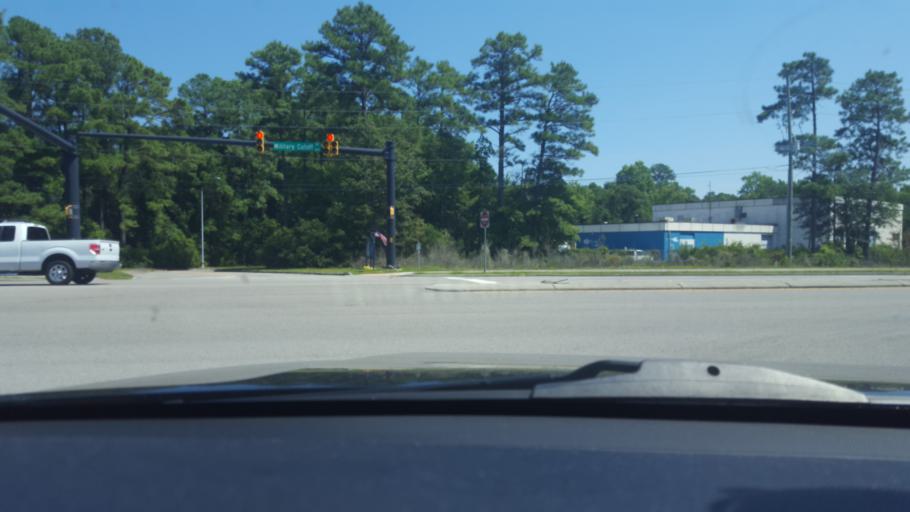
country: US
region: North Carolina
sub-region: New Hanover County
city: Ogden
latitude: 34.2541
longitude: -77.8267
